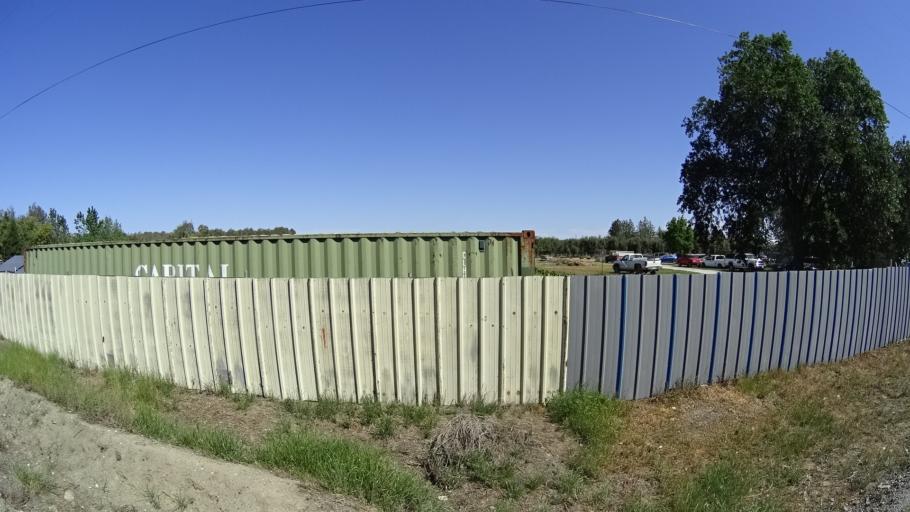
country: US
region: California
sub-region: Glenn County
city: Orland
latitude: 39.7584
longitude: -122.2036
